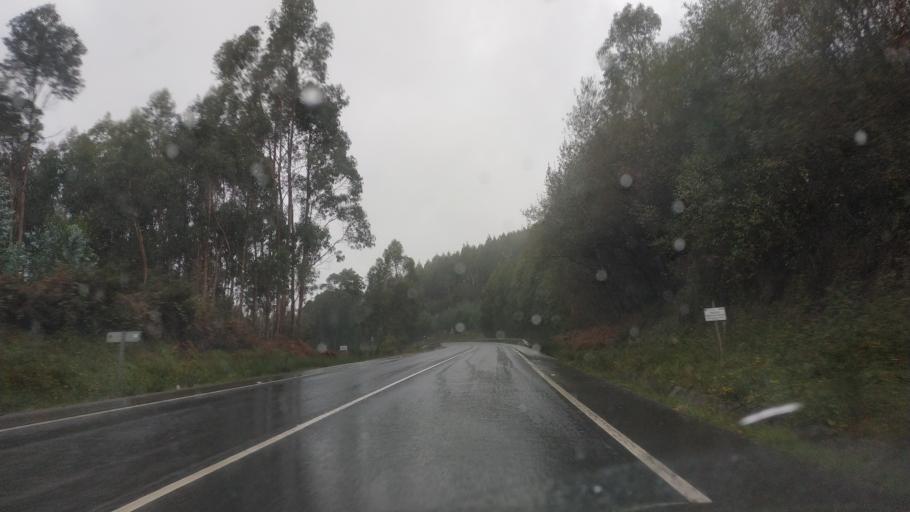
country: ES
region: Galicia
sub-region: Provincia da Coruna
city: Cerceda
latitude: 43.1649
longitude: -8.5183
